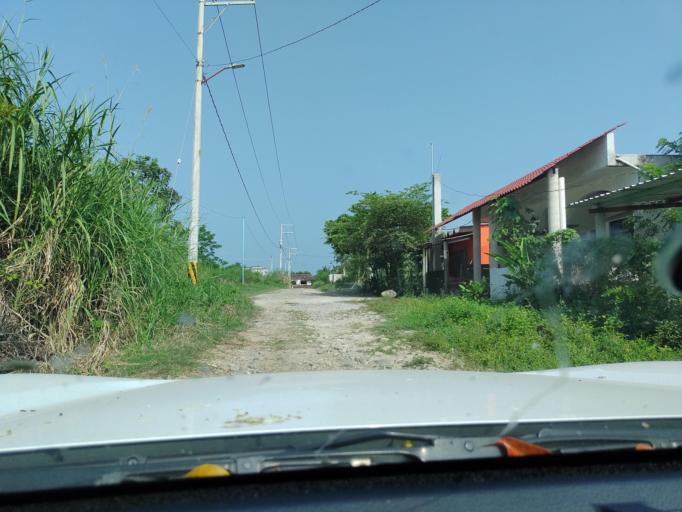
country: MX
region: Veracruz
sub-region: Martinez de la Torre
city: El Progreso
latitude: 20.0758
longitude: -97.0053
